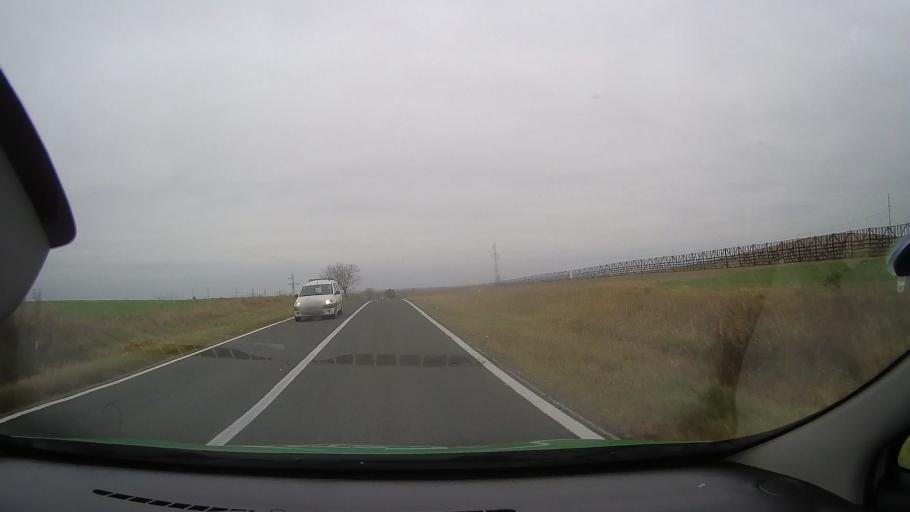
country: RO
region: Constanta
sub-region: Comuna Saraiu
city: Saraiu
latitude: 44.7111
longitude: 28.1177
